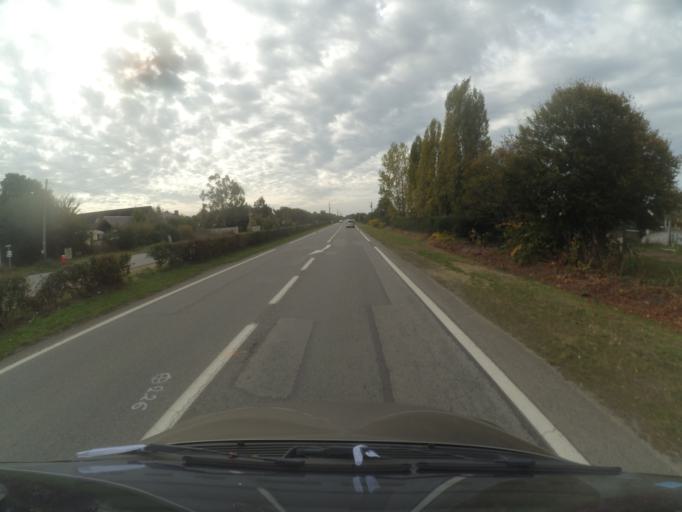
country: FR
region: Brittany
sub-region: Departement du Morbihan
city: Merlevenez
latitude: 47.7367
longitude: -3.2273
